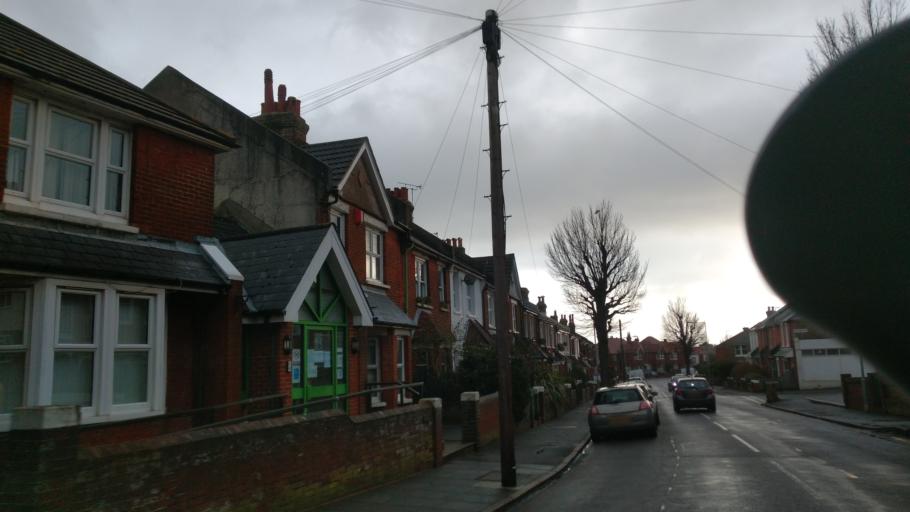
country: GB
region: England
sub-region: East Sussex
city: Eastbourne
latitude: 50.7767
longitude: 0.2574
